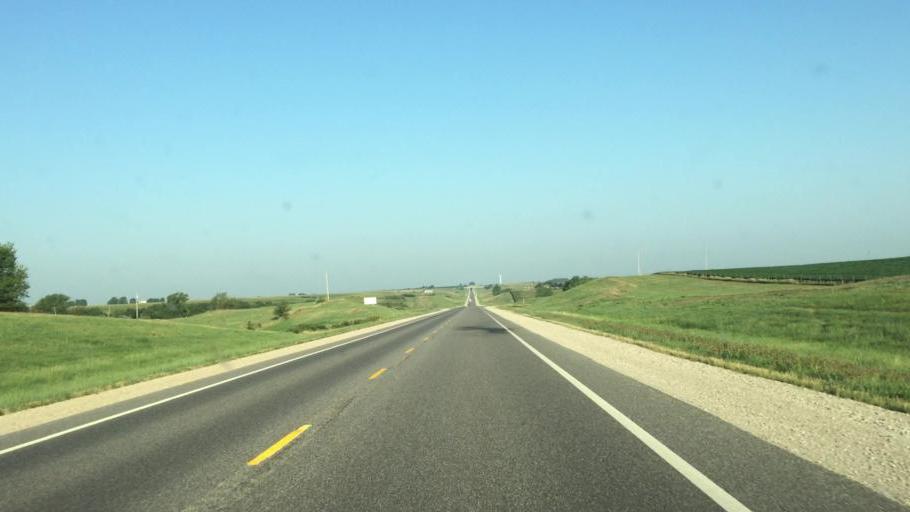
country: US
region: Kansas
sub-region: Doniphan County
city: Highland
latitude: 39.8422
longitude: -95.2989
